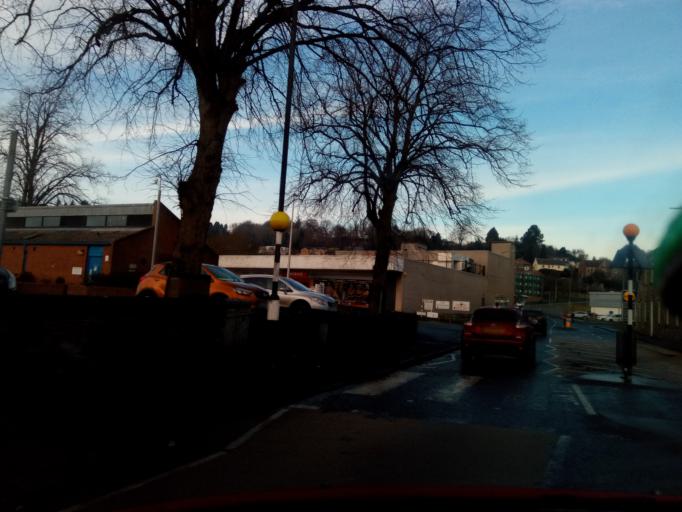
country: GB
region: Scotland
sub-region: The Scottish Borders
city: Hawick
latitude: 55.4231
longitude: -2.7902
